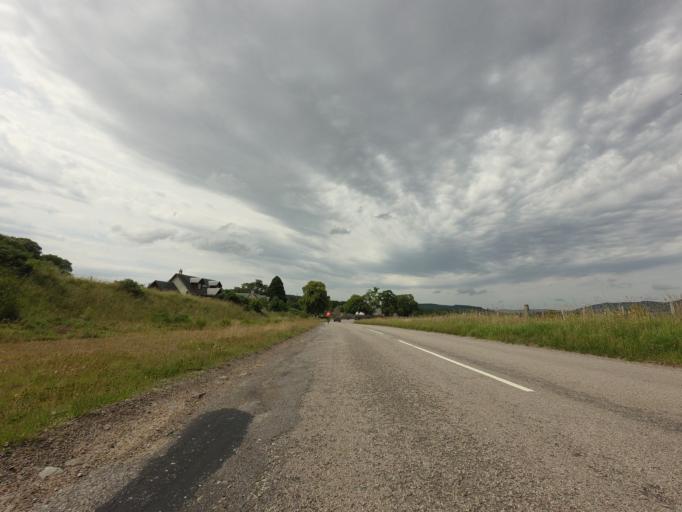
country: GB
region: Scotland
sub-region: Highland
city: Alness
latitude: 57.8717
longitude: -4.3506
